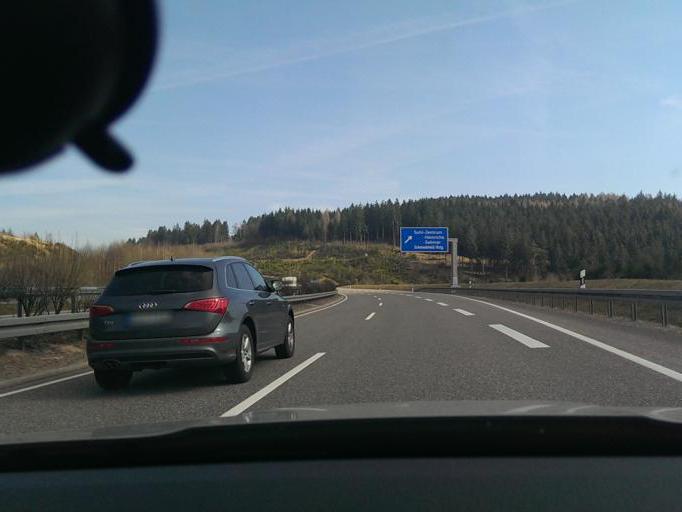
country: DE
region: Thuringia
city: Suhl
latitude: 50.5870
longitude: 10.6654
